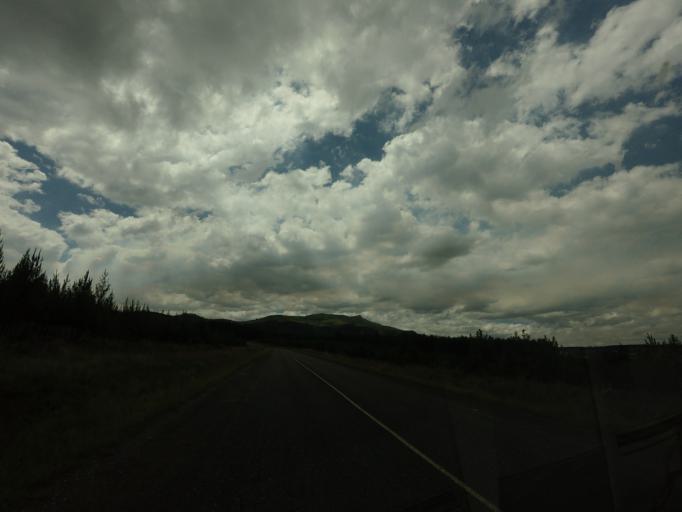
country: ZA
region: Mpumalanga
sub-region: Ehlanzeni District
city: Graksop
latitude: -24.9745
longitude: 30.8077
